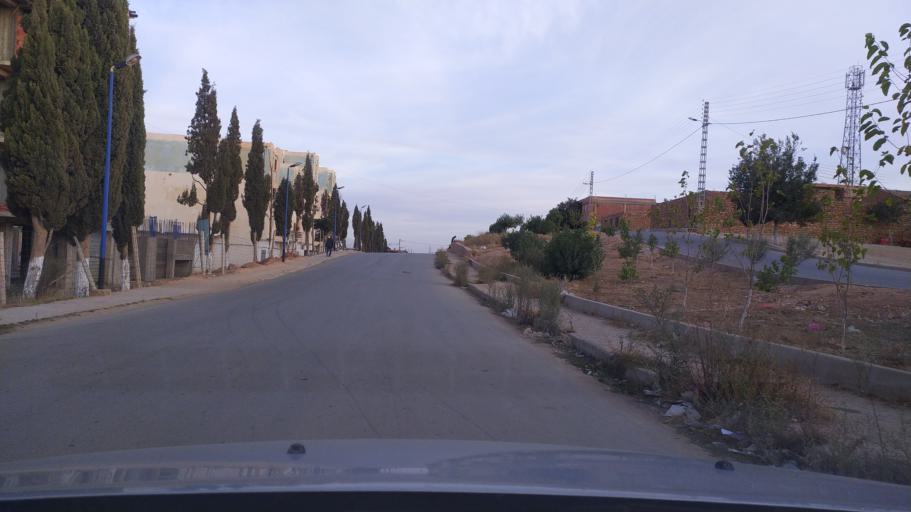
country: DZ
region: Tiaret
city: Frenda
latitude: 34.8948
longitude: 1.2394
